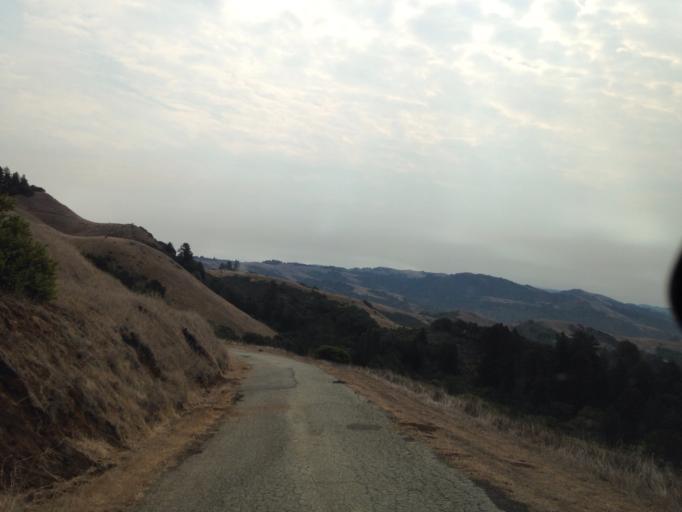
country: US
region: California
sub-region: San Mateo County
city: Portola Valley
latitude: 37.3669
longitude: -122.3024
